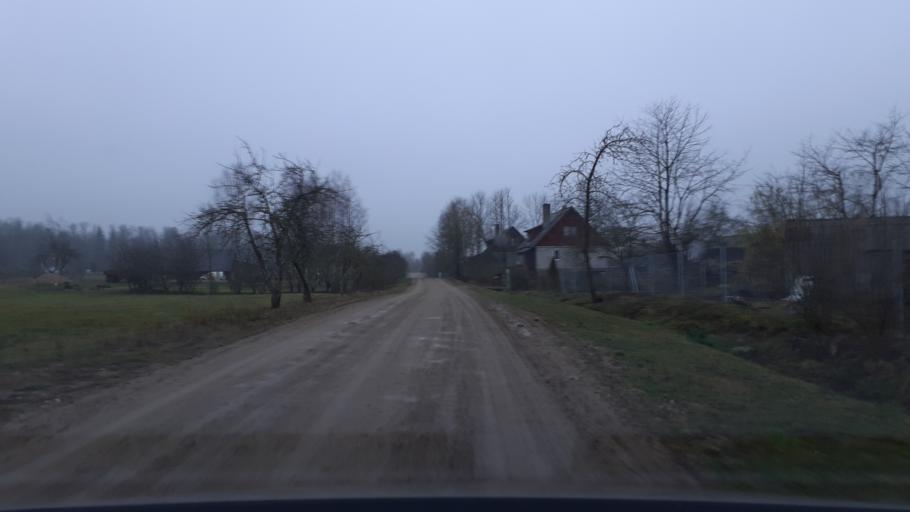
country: LV
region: Talsu Rajons
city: Sabile
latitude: 56.9570
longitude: 22.4040
